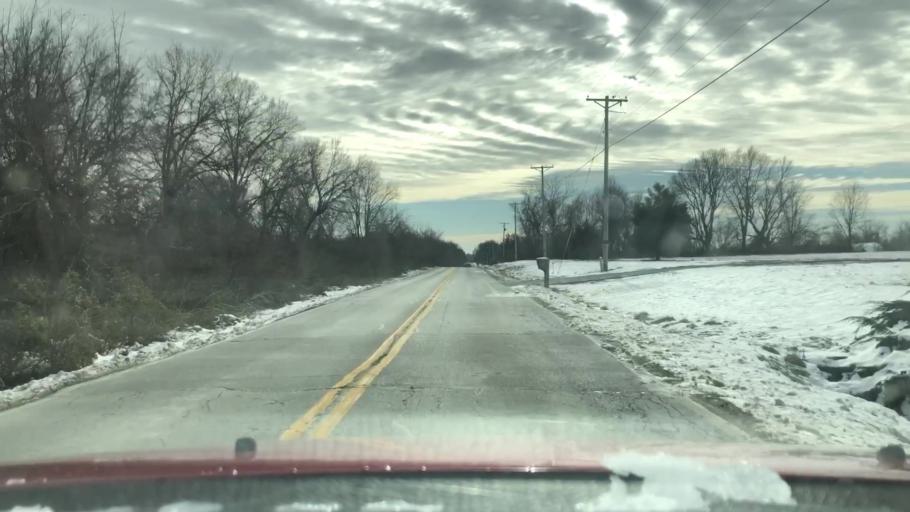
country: US
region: Missouri
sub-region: Jackson County
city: Greenwood
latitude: 38.8725
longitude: -94.3415
